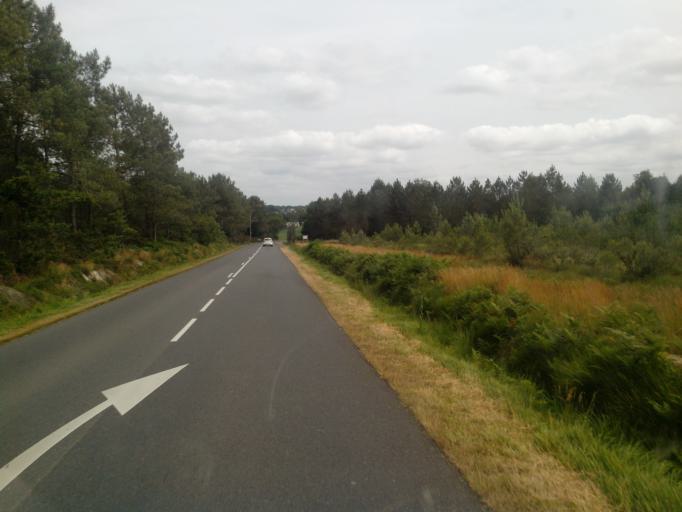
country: FR
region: Brittany
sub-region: Departement d'Ille-et-Vilaine
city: Plelan-le-Grand
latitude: 48.0083
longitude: -2.1241
